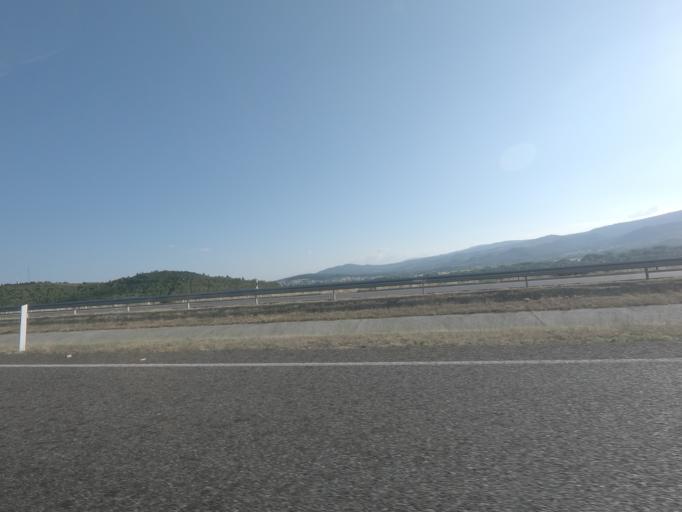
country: ES
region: Galicia
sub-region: Provincia de Ourense
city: Oimbra
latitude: 41.8642
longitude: -7.4284
